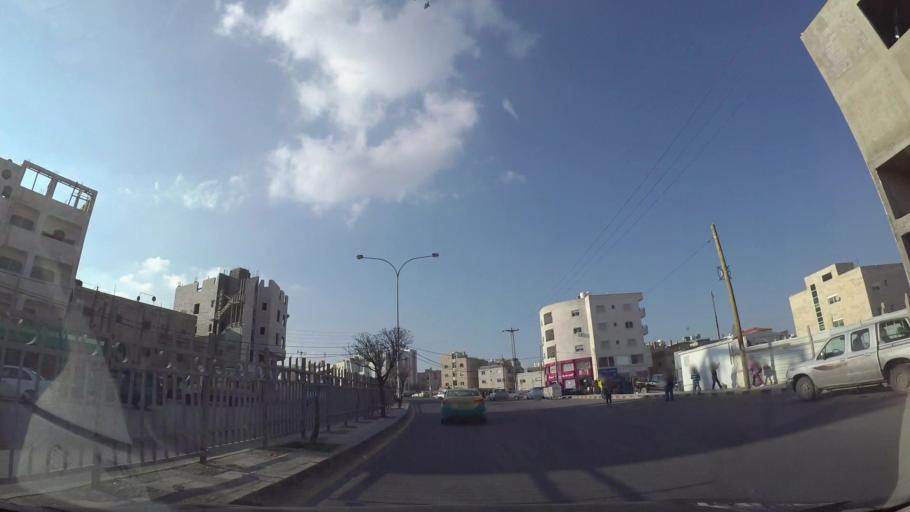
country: JO
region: Amman
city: Amman
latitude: 31.9783
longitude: 35.9436
